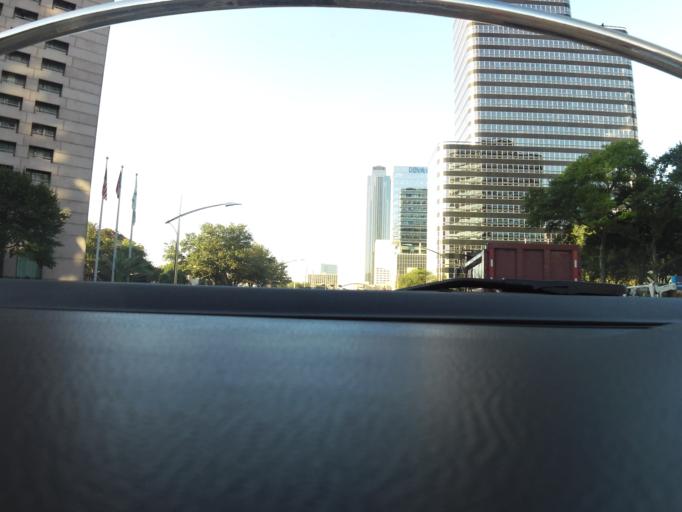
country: US
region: Texas
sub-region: Harris County
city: West University Place
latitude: 29.7461
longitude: -95.4611
